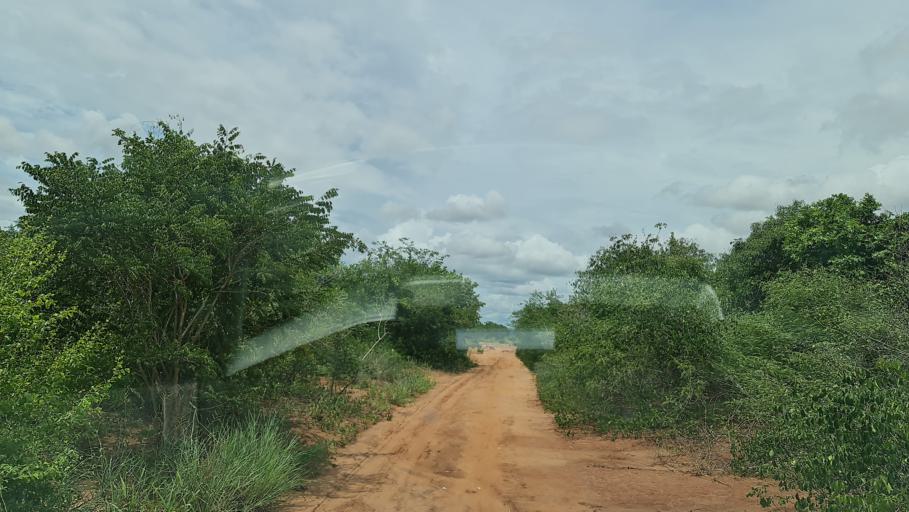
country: MZ
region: Nampula
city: Nacala
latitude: -14.7900
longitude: 39.9696
